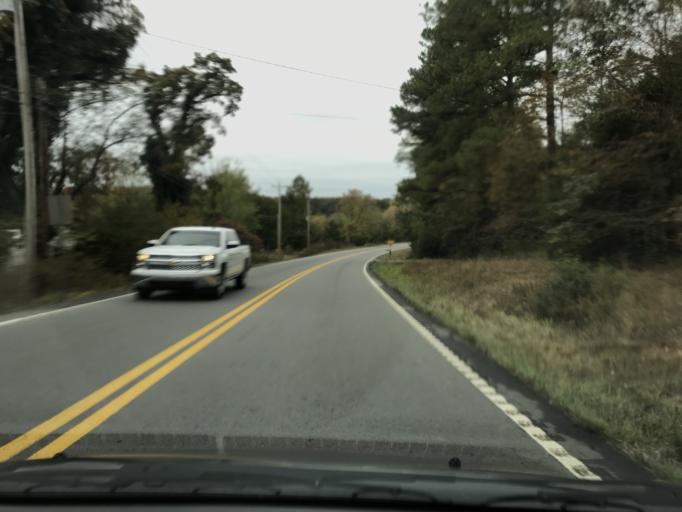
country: US
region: Tennessee
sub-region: Hamilton County
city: Sale Creek
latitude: 35.3518
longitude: -84.9900
